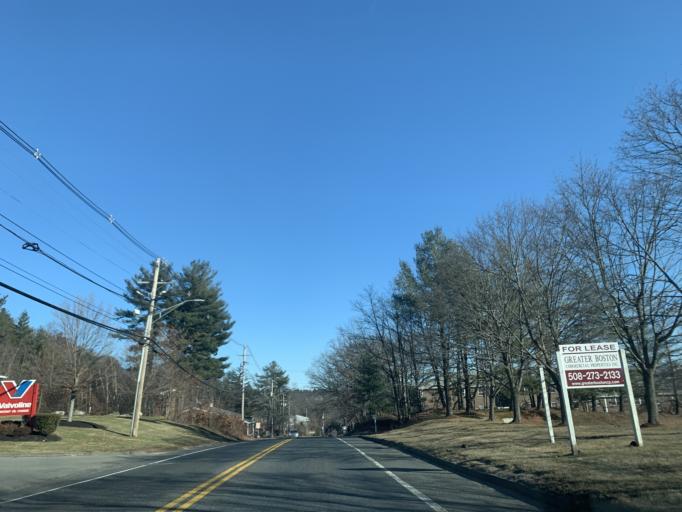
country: US
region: Massachusetts
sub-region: Middlesex County
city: Marlborough
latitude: 42.3492
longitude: -71.5224
